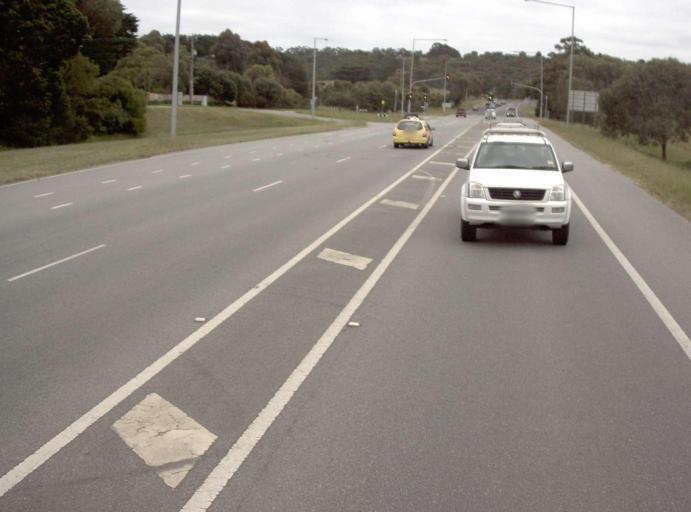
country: AU
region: Victoria
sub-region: Mornington Peninsula
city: Mount Martha
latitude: -38.2975
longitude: 145.0319
